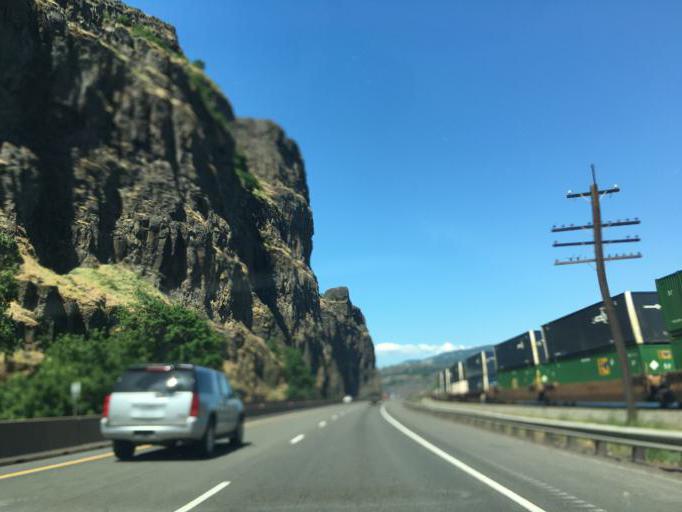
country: US
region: Oregon
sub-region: Wasco County
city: Chenoweth
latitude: 45.6872
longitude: -121.2983
